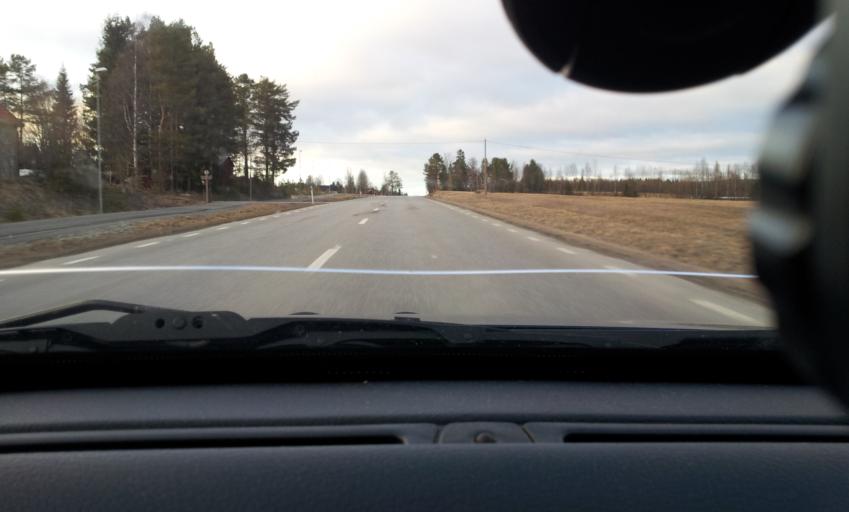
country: SE
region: Jaemtland
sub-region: Bergs Kommun
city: Hoverberg
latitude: 62.6953
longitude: 14.4055
